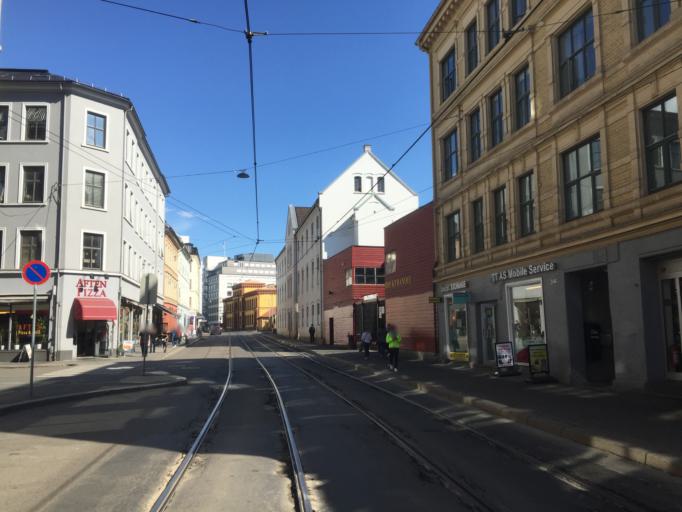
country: NO
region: Oslo
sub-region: Oslo
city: Oslo
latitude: 59.9149
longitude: 10.7543
